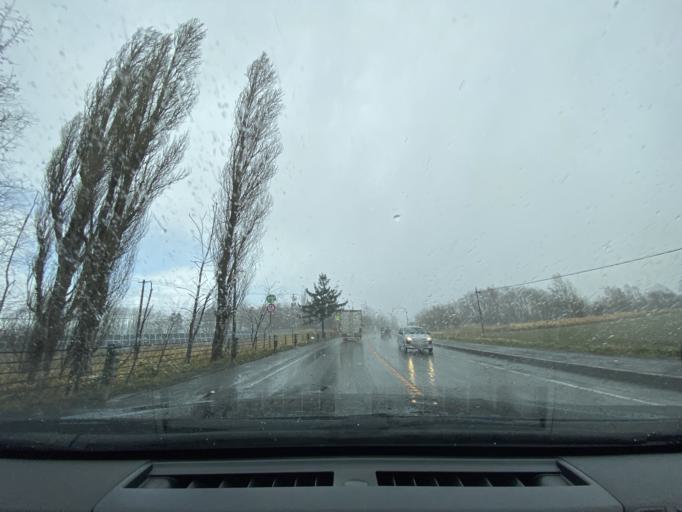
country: JP
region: Hokkaido
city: Takikawa
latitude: 43.6418
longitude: 141.9494
